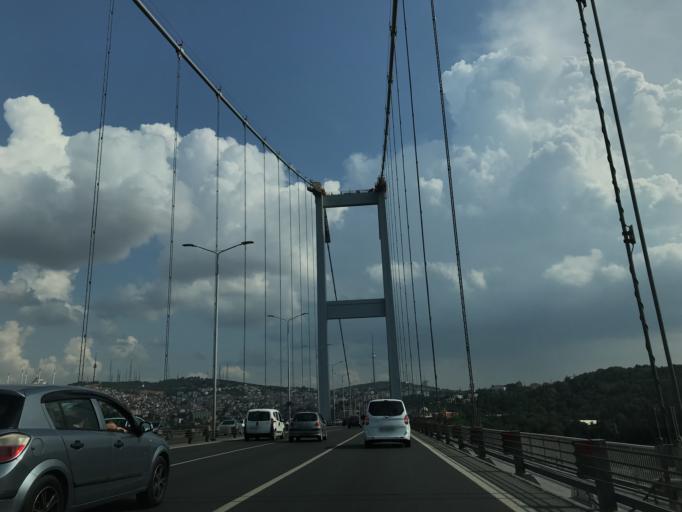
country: TR
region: Istanbul
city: UEskuedar
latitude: 41.0436
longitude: 29.0362
